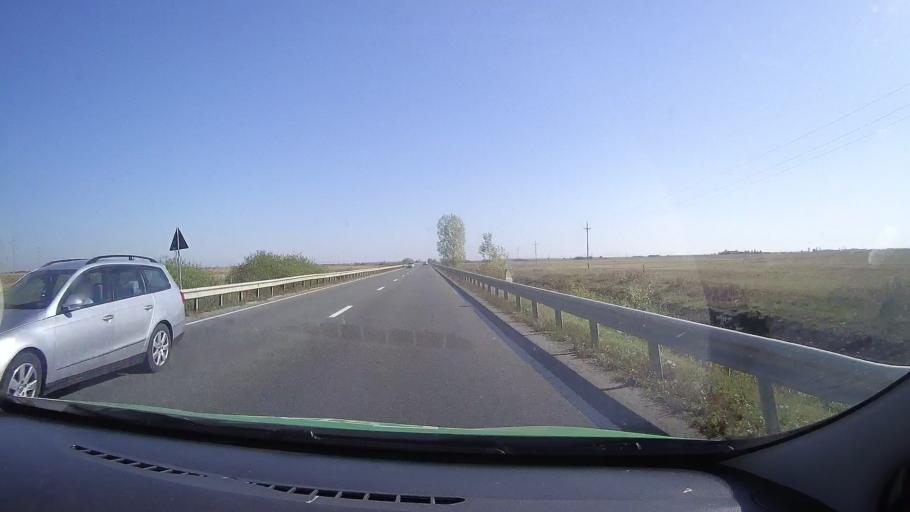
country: RO
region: Satu Mare
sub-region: Comuna Capleni
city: Capleni
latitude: 47.6852
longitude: 22.5295
